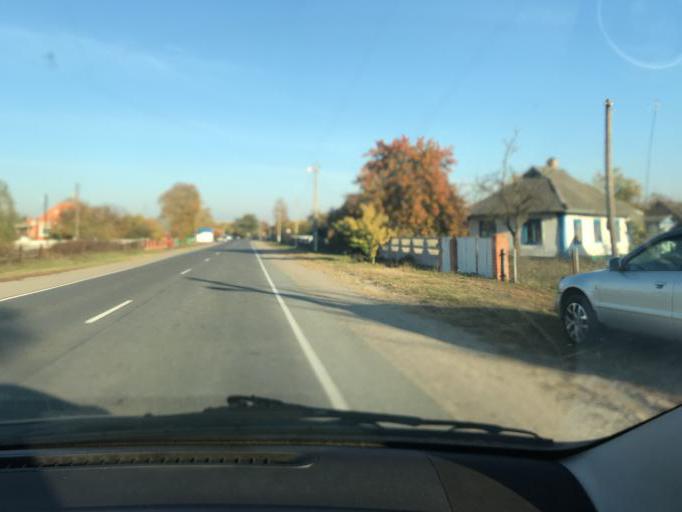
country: BY
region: Brest
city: Stolin
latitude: 51.8468
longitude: 26.7797
